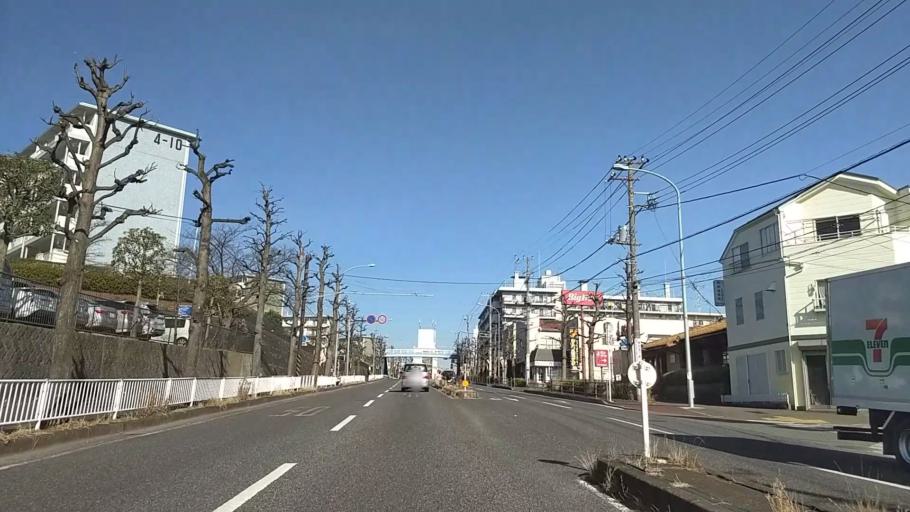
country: JP
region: Kanagawa
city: Kamakura
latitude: 35.3746
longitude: 139.5979
